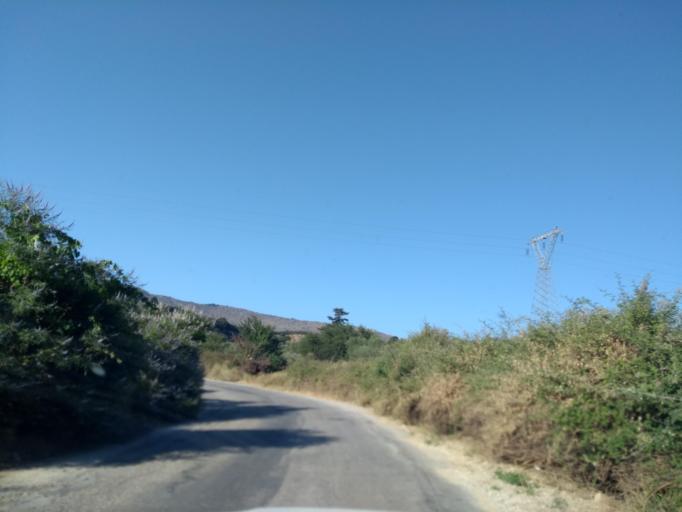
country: GR
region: Crete
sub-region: Nomos Chanias
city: Georgioupolis
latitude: 35.3661
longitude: 24.2278
